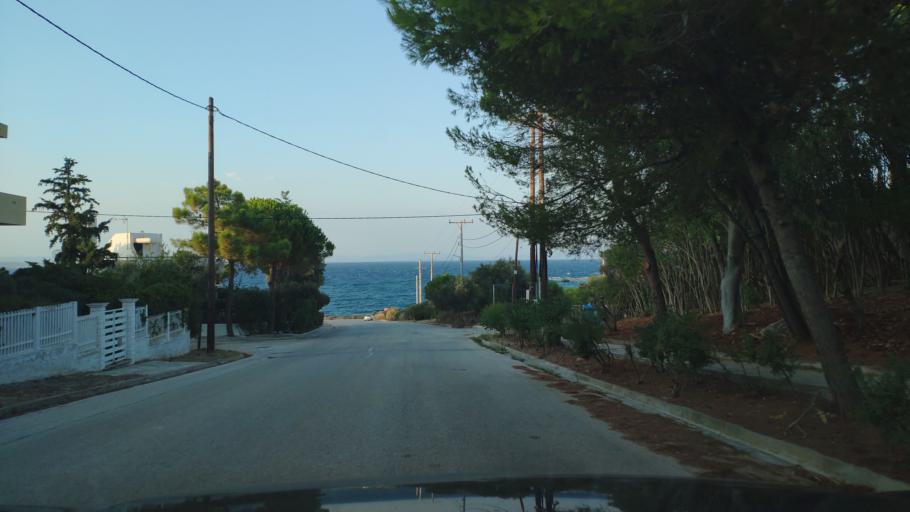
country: GR
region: Attica
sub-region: Nomarchia Anatolikis Attikis
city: Limin Mesoyaias
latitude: 37.9197
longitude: 24.0243
